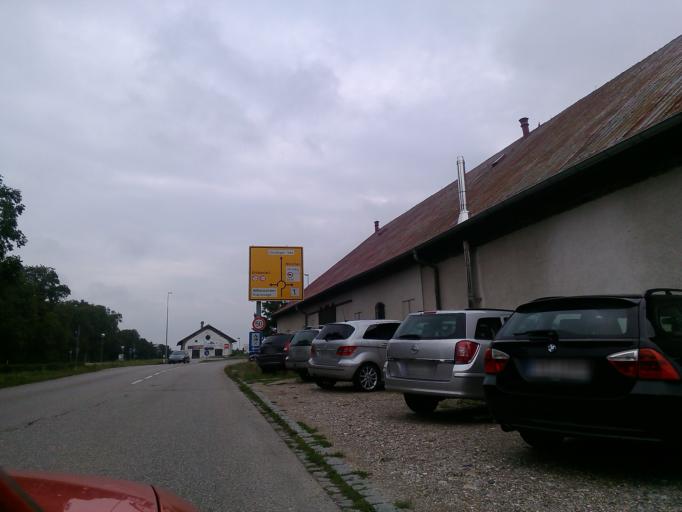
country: DE
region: Bavaria
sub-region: Upper Bavaria
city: Grobenzell
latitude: 48.2229
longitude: 11.3542
